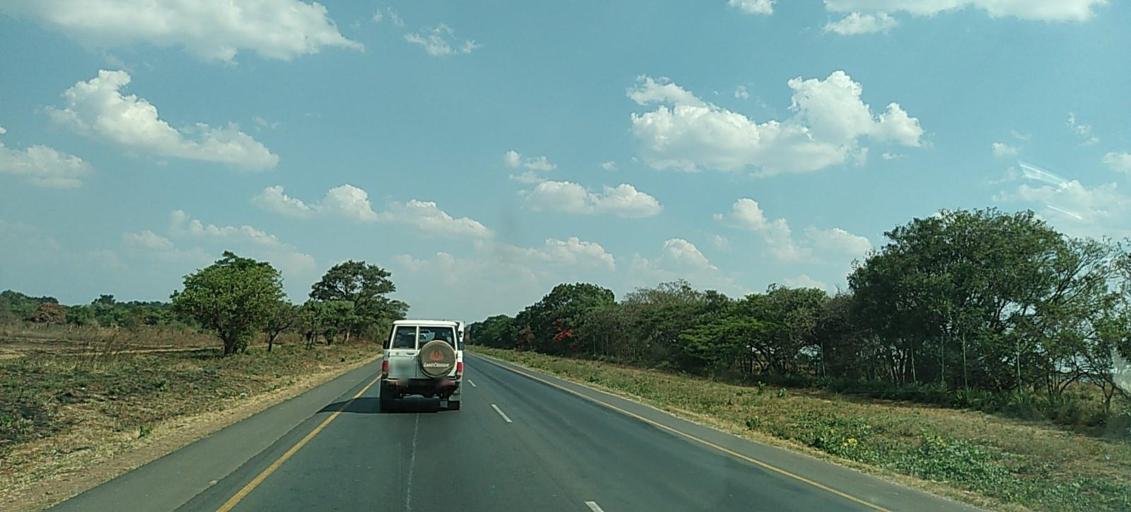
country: ZM
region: Central
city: Chibombo
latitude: -14.8831
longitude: 28.0623
